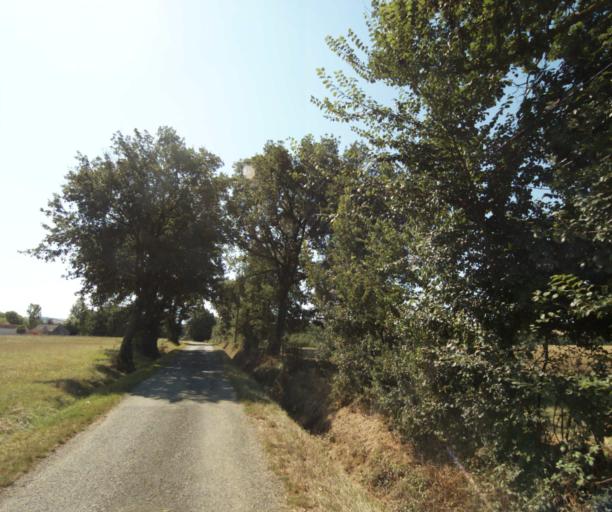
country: FR
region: Midi-Pyrenees
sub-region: Departement de l'Ariege
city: Lezat-sur-Leze
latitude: 43.2992
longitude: 1.3286
